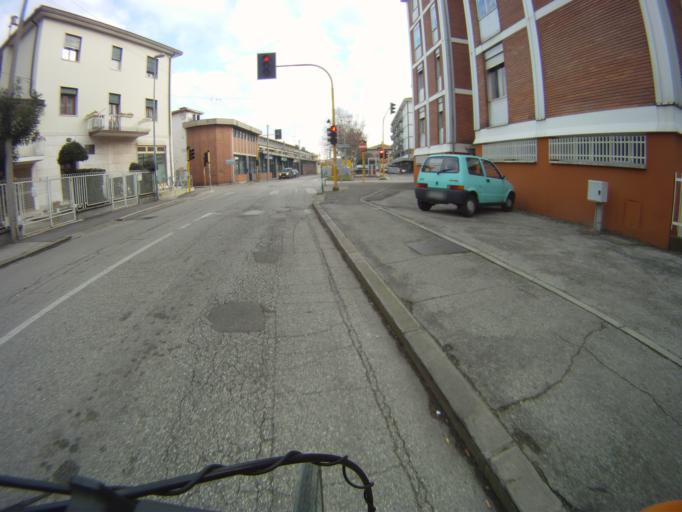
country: IT
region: Veneto
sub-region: Provincia di Padova
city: Padova
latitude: 45.3905
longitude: 11.8901
